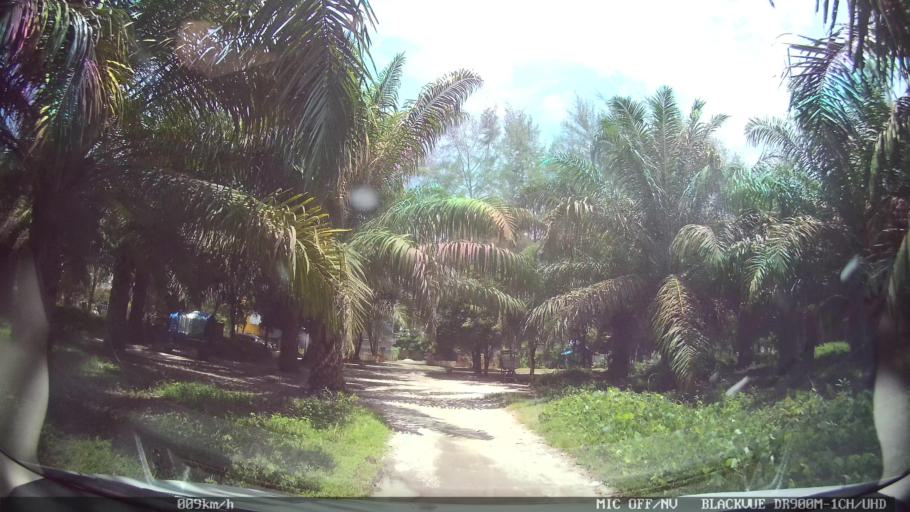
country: ID
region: North Sumatra
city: Percut
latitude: 3.5400
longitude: 98.8723
